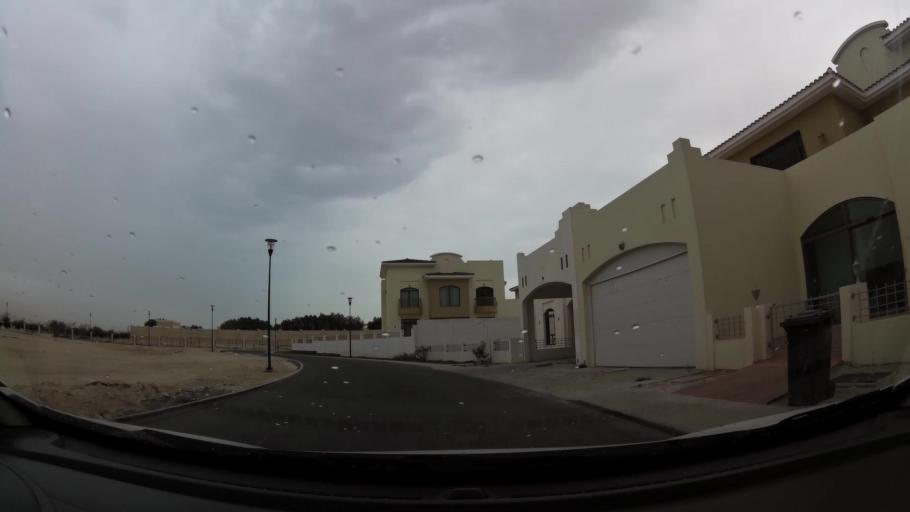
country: BH
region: Northern
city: Ar Rifa'
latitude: 26.0912
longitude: 50.5595
